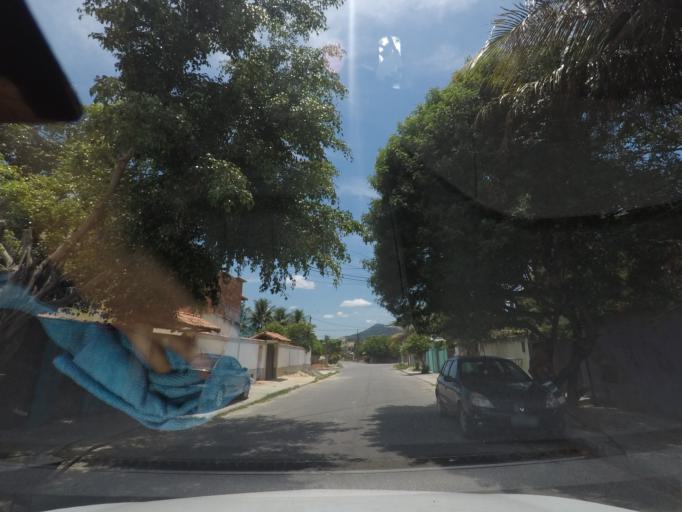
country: BR
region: Rio de Janeiro
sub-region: Marica
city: Marica
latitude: -22.9240
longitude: -42.8232
